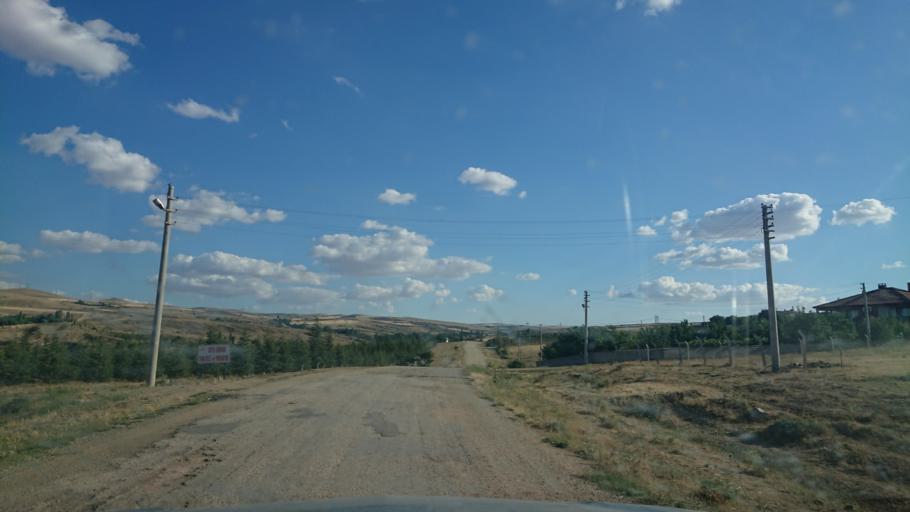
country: TR
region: Aksaray
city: Sariyahsi
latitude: 38.9532
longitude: 33.8831
